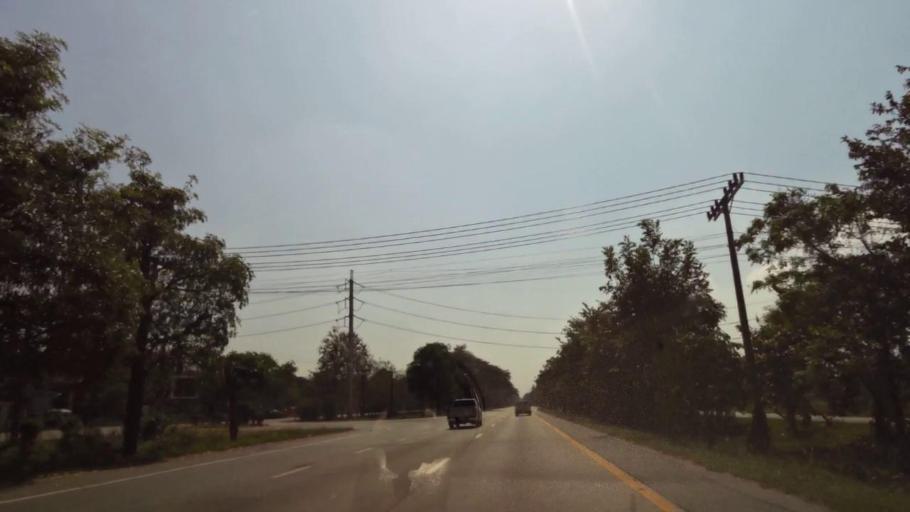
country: TH
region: Phichit
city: Wachira Barami
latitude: 16.5755
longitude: 100.1482
